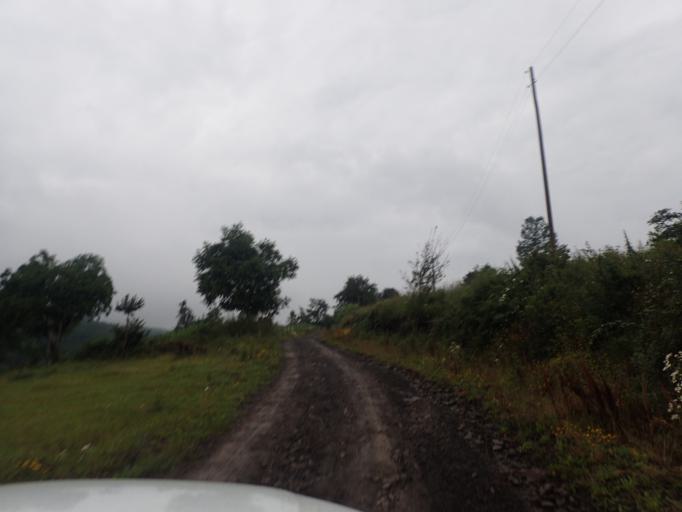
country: TR
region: Ordu
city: Akkus
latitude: 40.8083
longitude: 37.1028
